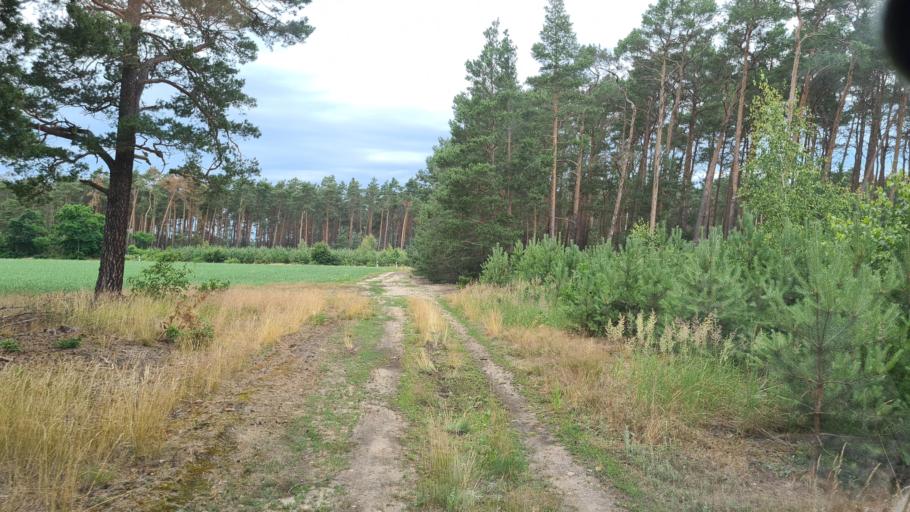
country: DE
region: Brandenburg
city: Crinitz
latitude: 51.7208
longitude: 13.8425
